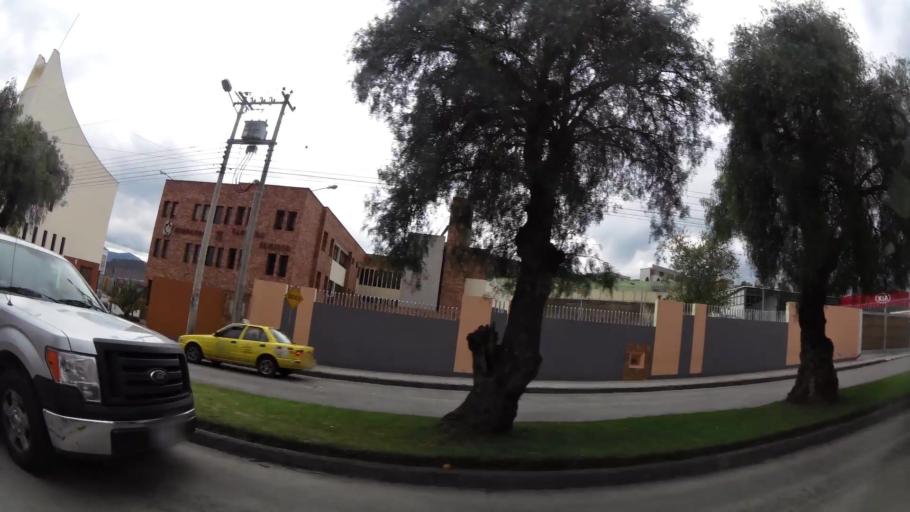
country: EC
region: Tungurahua
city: Ambato
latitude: -1.2381
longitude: -78.6147
